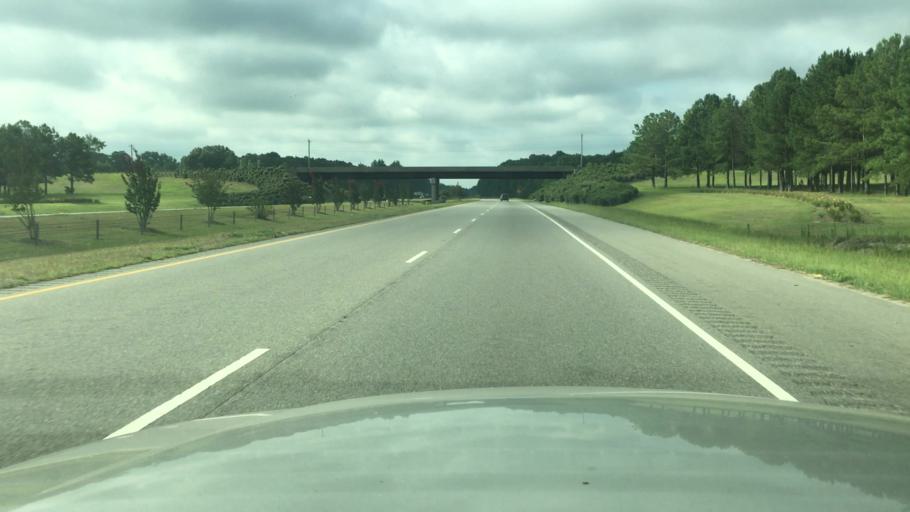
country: US
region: North Carolina
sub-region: Cumberland County
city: Fayetteville
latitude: 35.0115
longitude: -78.8696
